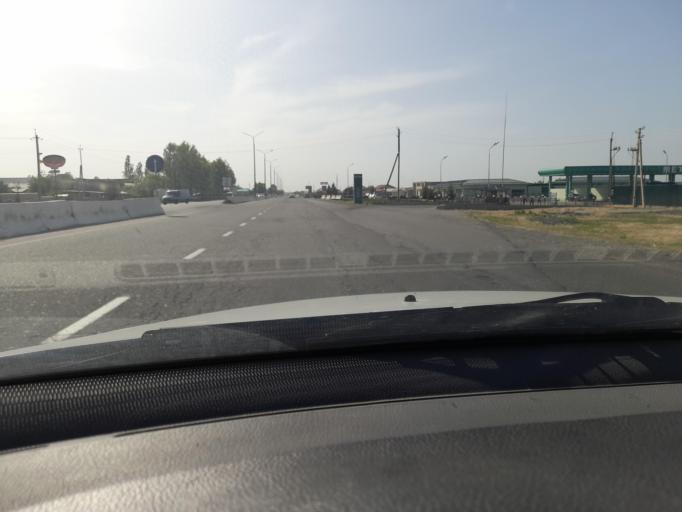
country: UZ
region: Samarqand
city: Kattaqo'rg'on
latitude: 39.9177
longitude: 66.3036
